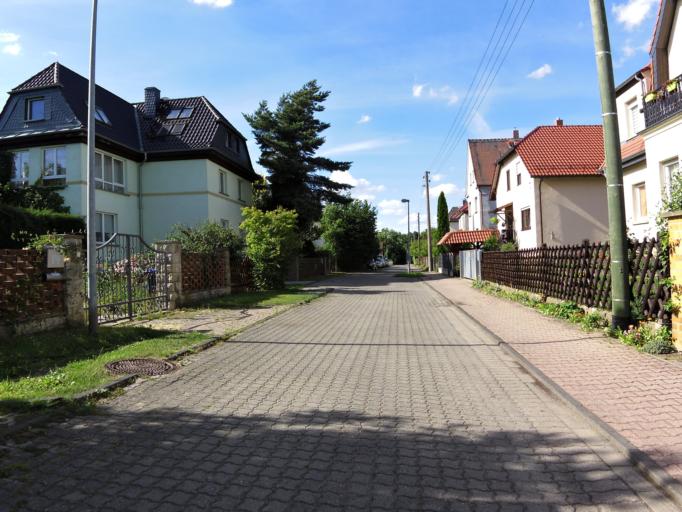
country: DE
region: Saxony
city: Taucha
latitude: 51.3228
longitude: 12.4592
